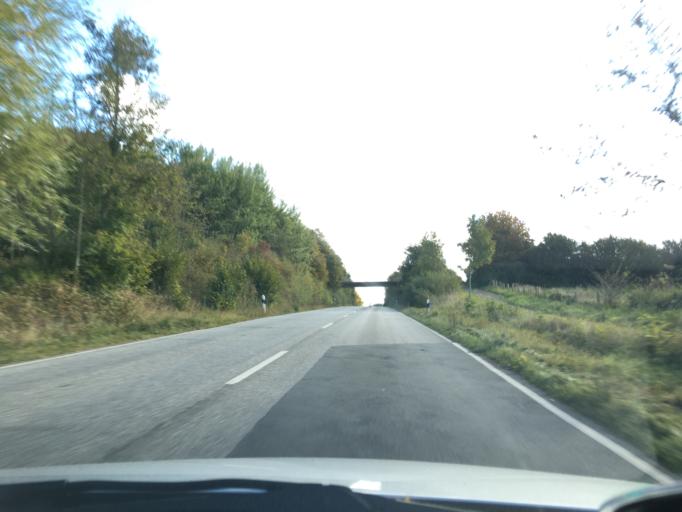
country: DE
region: Schleswig-Holstein
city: Melsdorf
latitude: 54.3037
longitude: 10.0250
